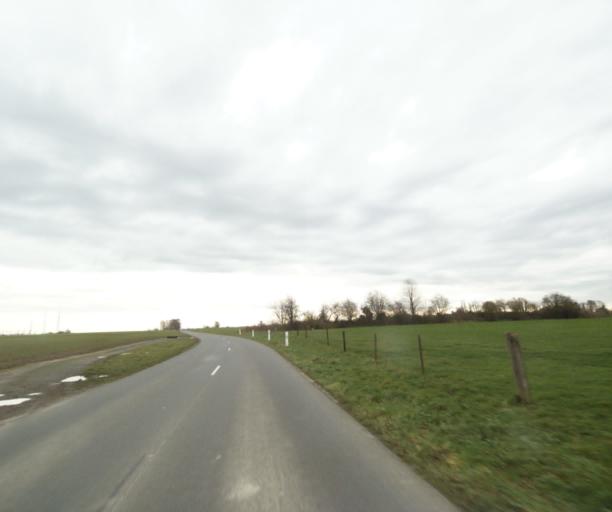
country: FR
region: Nord-Pas-de-Calais
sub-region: Departement du Nord
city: Saultain
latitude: 50.3578
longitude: 3.5948
